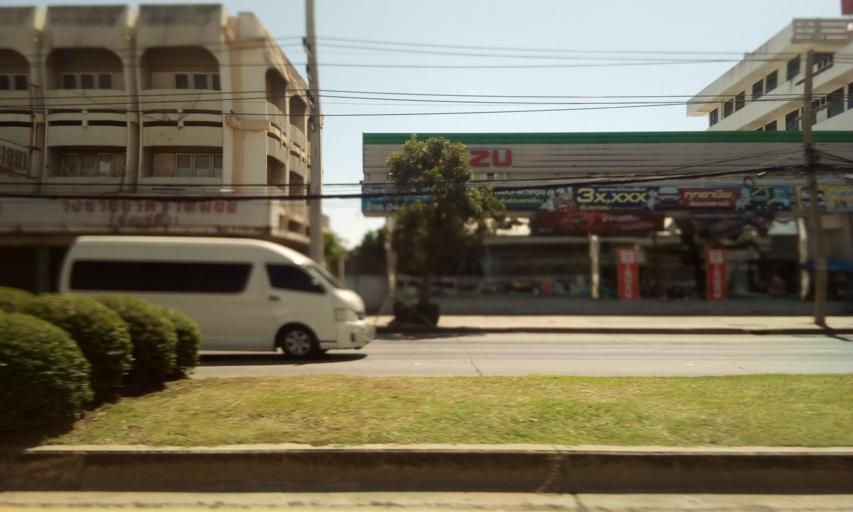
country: TH
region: Nakhon Ratchasima
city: Nakhon Ratchasima
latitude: 14.9795
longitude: 102.0857
